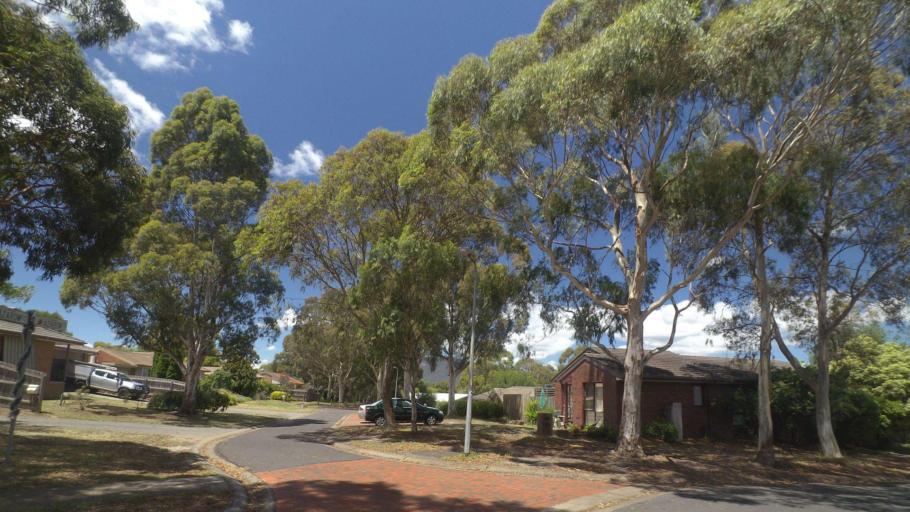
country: AU
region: Victoria
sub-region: Maroondah
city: Croydon South
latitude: -37.8178
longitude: 145.2815
